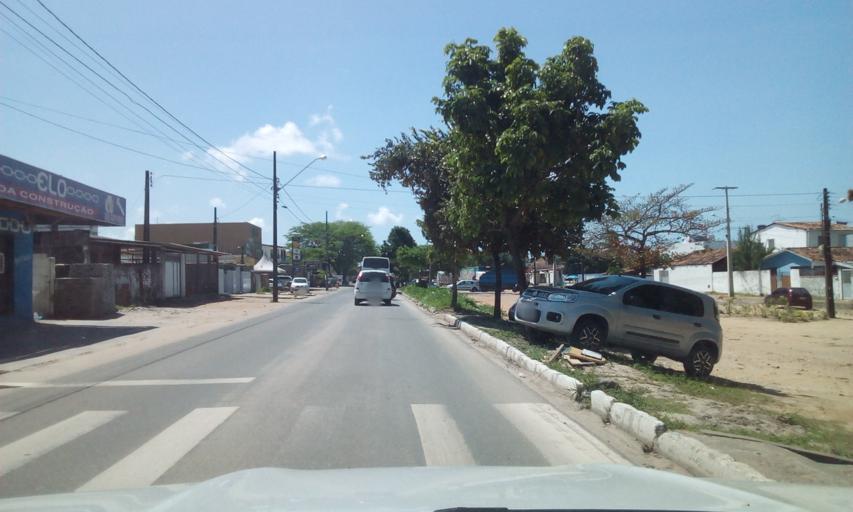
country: BR
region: Paraiba
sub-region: Conde
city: Conde
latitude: -7.2059
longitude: -34.8539
